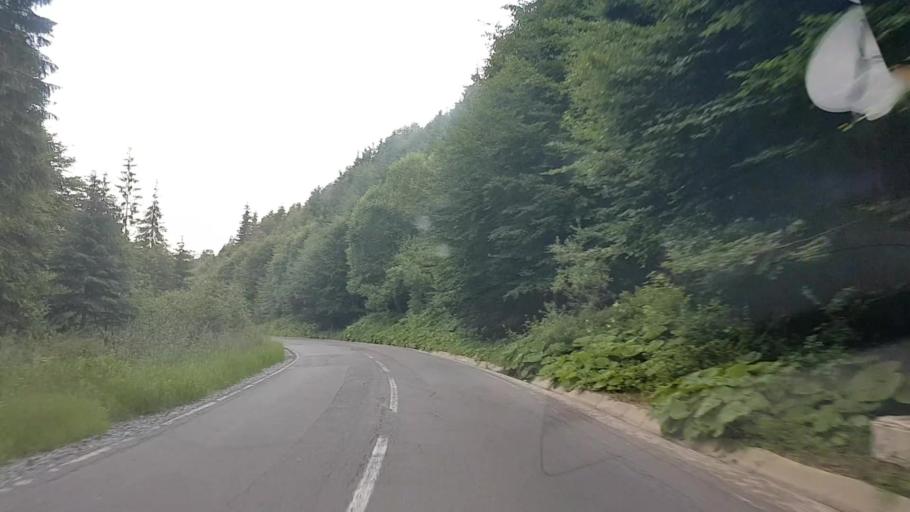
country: RO
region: Harghita
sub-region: Comuna Praid
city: Ocna de Sus
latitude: 46.6224
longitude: 25.2517
